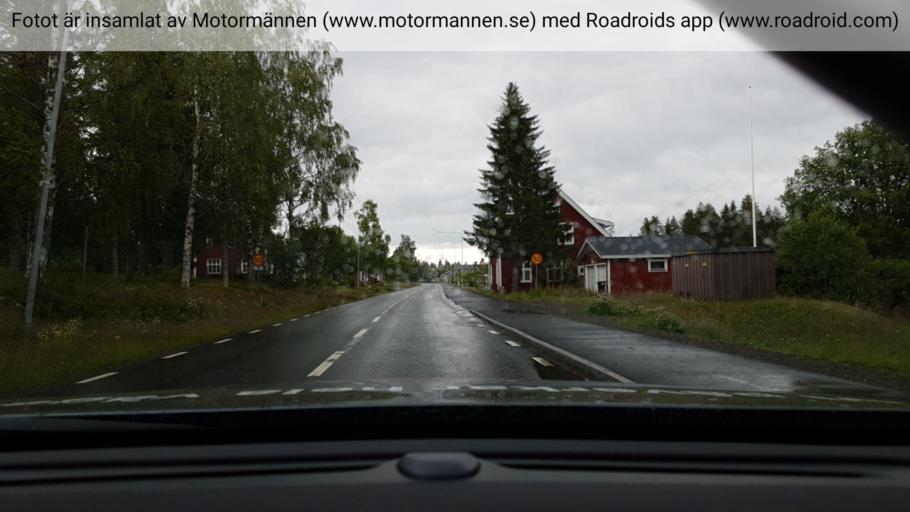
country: SE
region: Vaesterbotten
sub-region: Norsjo Kommun
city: Norsjoe
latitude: 65.2611
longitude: 19.6398
